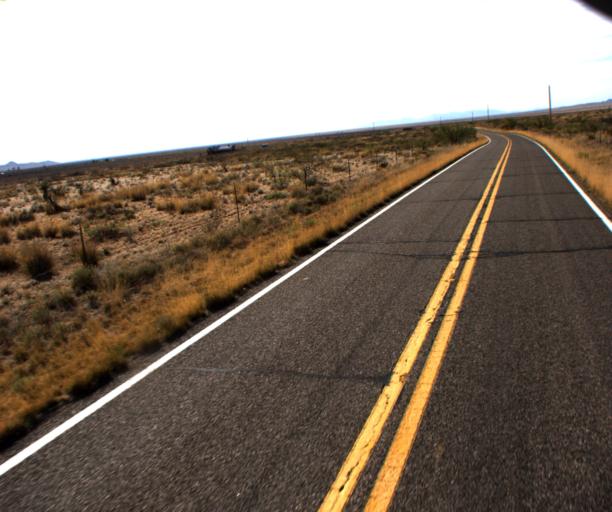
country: US
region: Arizona
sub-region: Cochise County
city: Willcox
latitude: 32.0339
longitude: -109.4729
